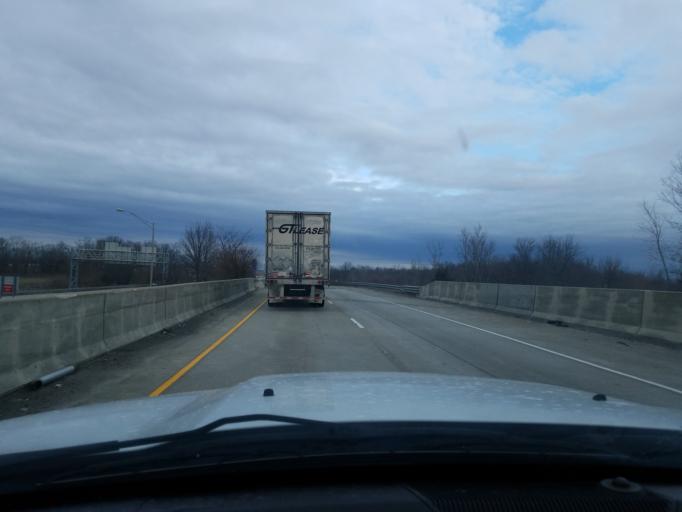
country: US
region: Indiana
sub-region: Boone County
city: Lebanon
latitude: 40.0636
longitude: -86.4941
